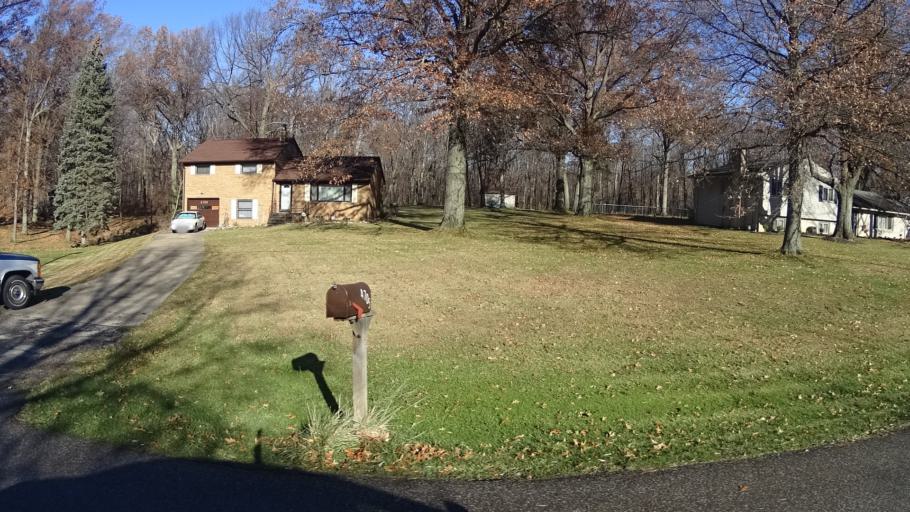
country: US
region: Ohio
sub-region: Lorain County
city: Sheffield
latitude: 41.4528
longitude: -82.0933
